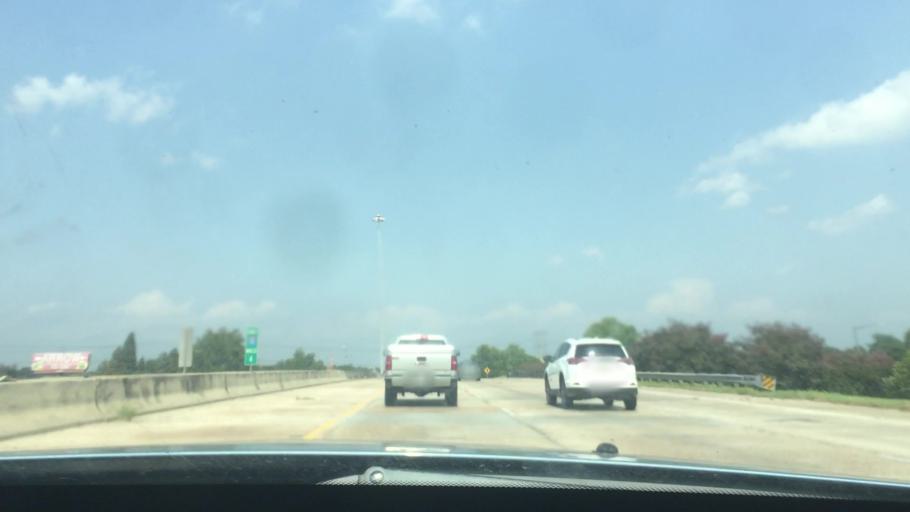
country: US
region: Louisiana
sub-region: East Baton Rouge Parish
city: Westminster
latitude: 30.4298
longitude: -91.0576
